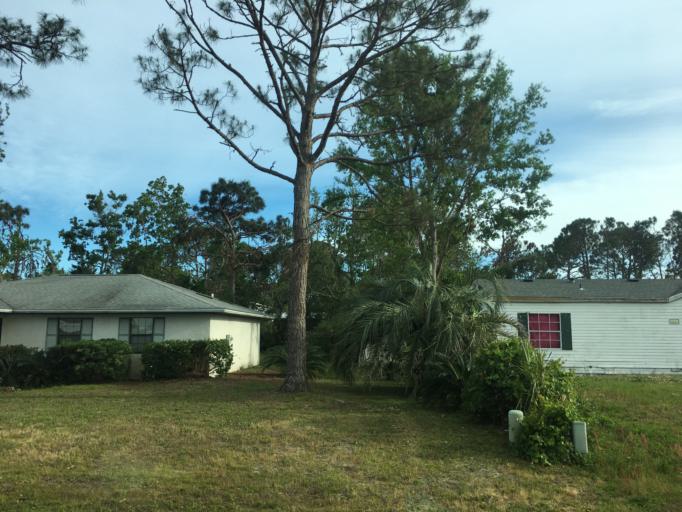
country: US
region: Florida
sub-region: Bay County
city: Upper Grand Lagoon
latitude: 30.1673
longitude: -85.7606
